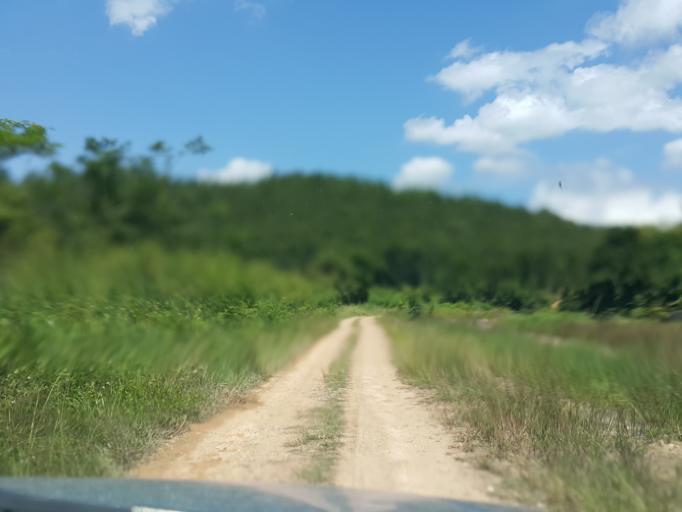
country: TH
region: Chiang Mai
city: San Kamphaeng
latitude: 18.7165
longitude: 99.1842
